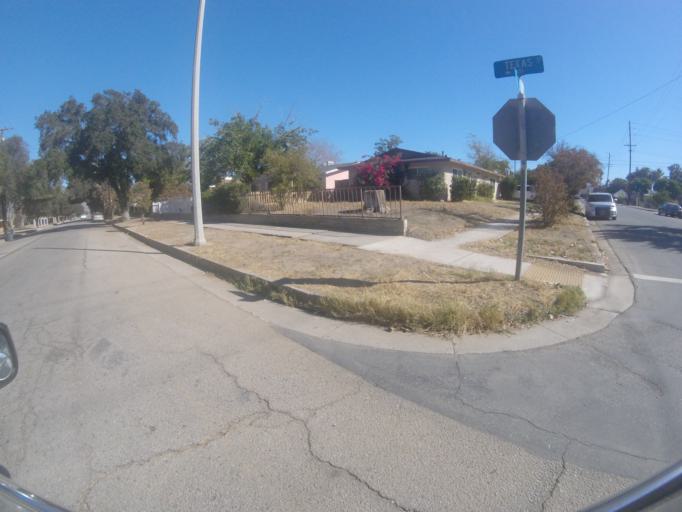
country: US
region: California
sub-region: San Bernardino County
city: Redlands
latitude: 34.0641
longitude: -117.1912
